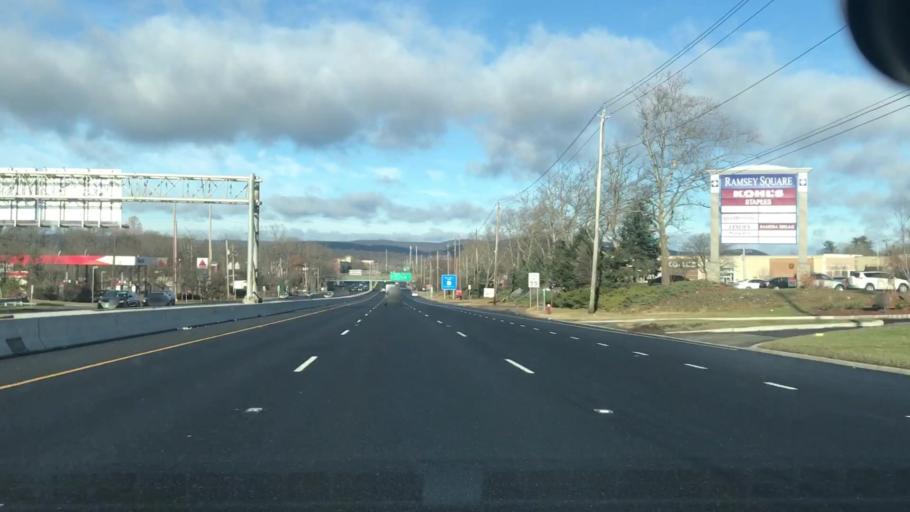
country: US
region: New Jersey
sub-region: Bergen County
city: Ramsey
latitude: 41.0707
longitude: -74.1383
